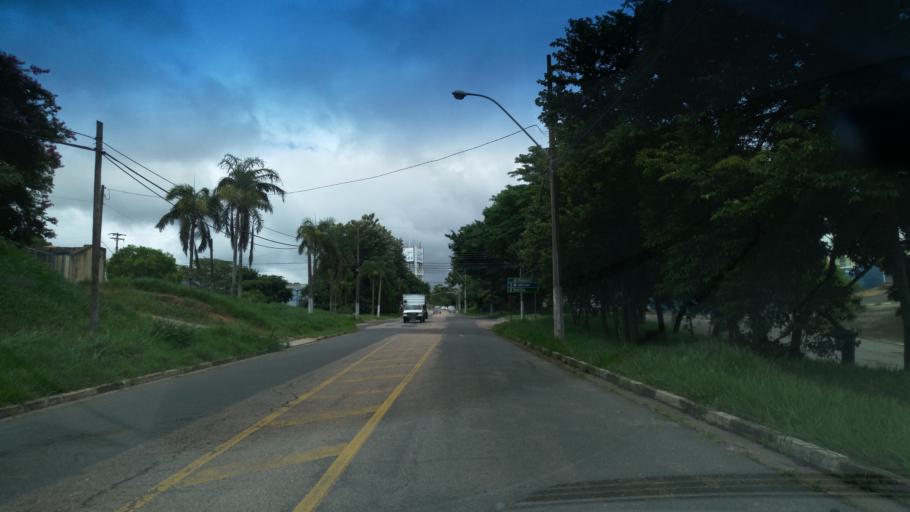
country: BR
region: Sao Paulo
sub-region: Valinhos
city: Valinhos
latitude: -22.9666
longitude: -46.9805
